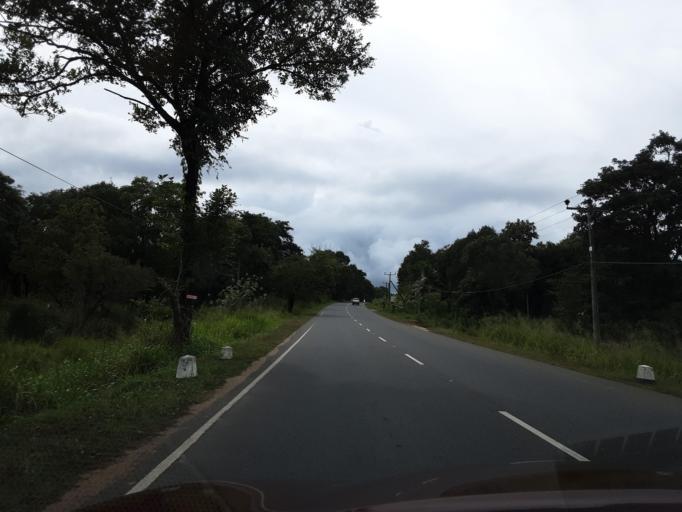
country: LK
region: Uva
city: Badulla
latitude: 7.3879
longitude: 81.1452
